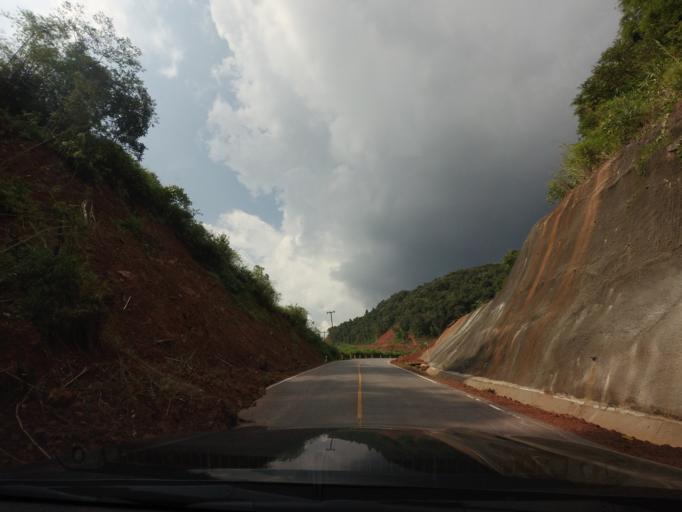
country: TH
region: Nan
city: Bo Kluea
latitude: 19.2411
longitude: 101.1816
